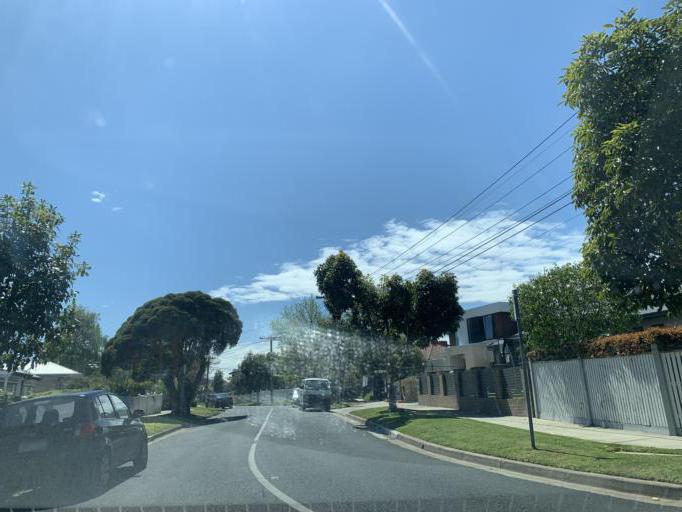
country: AU
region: Victoria
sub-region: Bayside
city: Moorabbin
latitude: -37.9438
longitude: 145.0353
